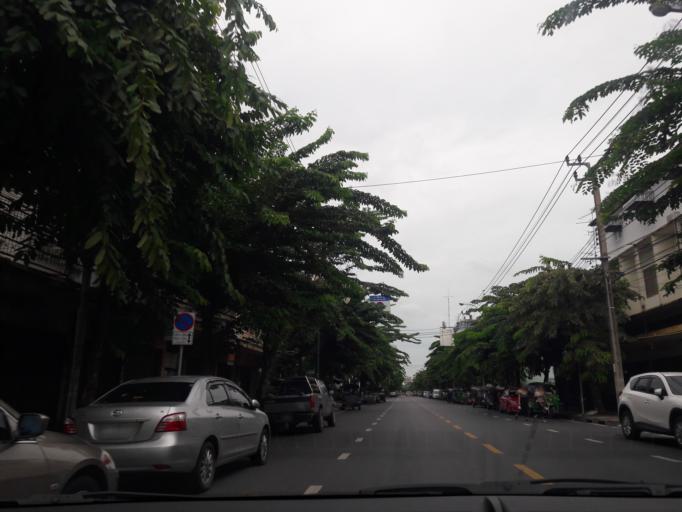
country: TH
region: Bangkok
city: Khlong San
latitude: 13.7300
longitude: 100.4970
